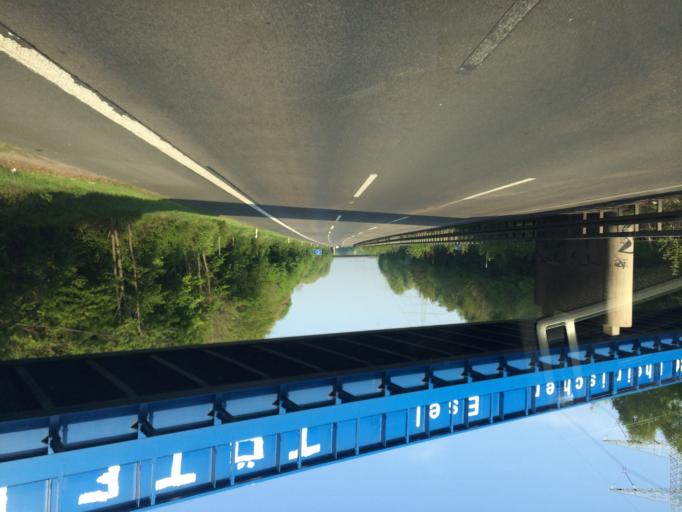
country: DE
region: North Rhine-Westphalia
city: Witten
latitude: 51.4585
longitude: 7.3439
